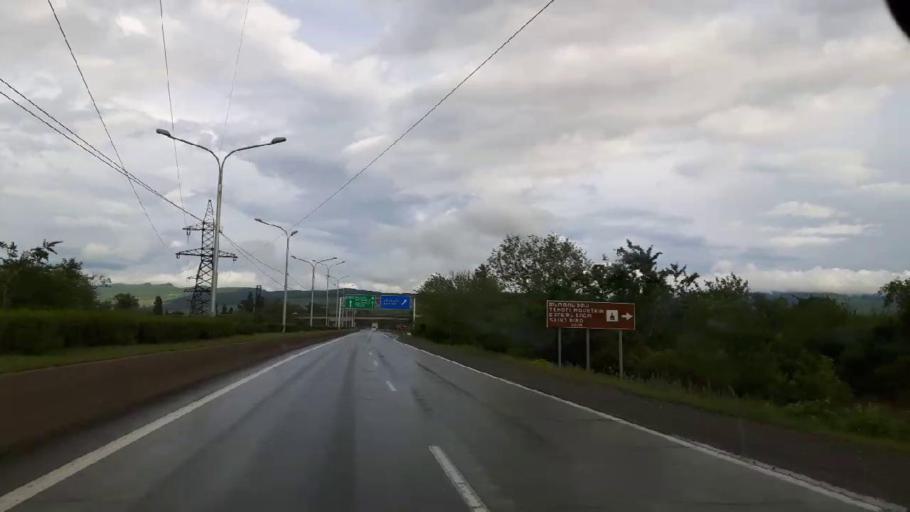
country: GE
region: Shida Kartli
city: Kaspi
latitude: 41.9149
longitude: 44.5569
